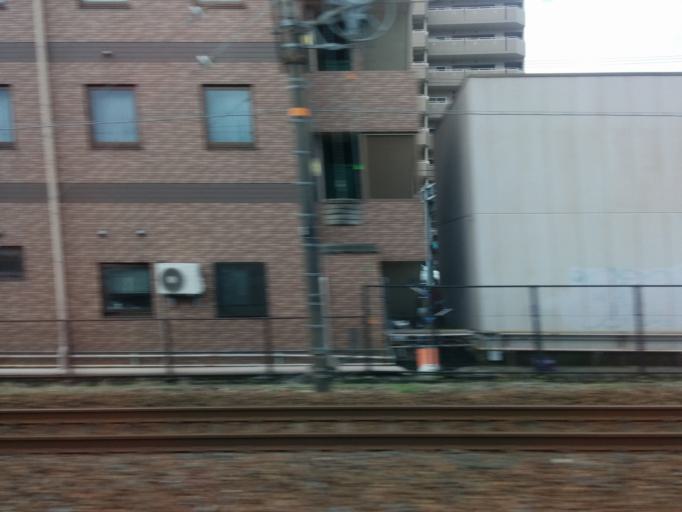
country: JP
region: Shiga Prefecture
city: Otsu-shi
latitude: 35.0025
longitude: 135.8701
